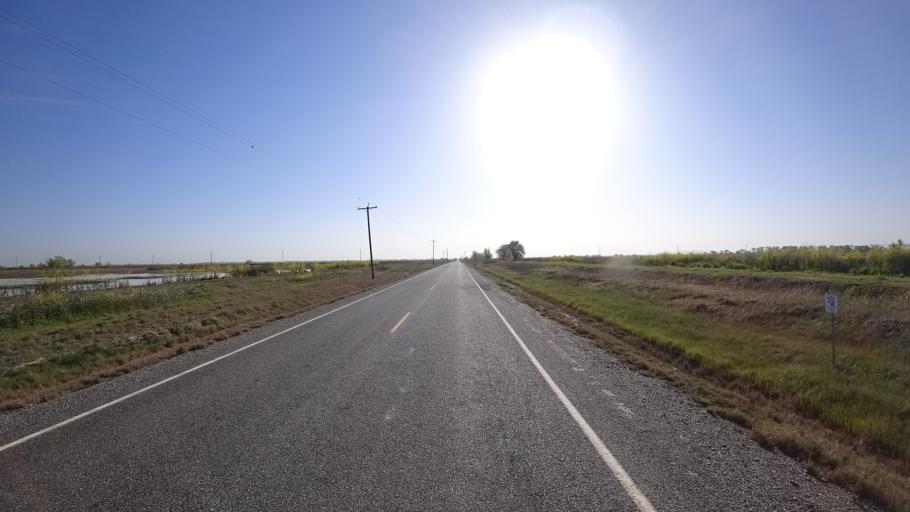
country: US
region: California
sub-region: Glenn County
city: Willows
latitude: 39.4071
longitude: -122.1871
